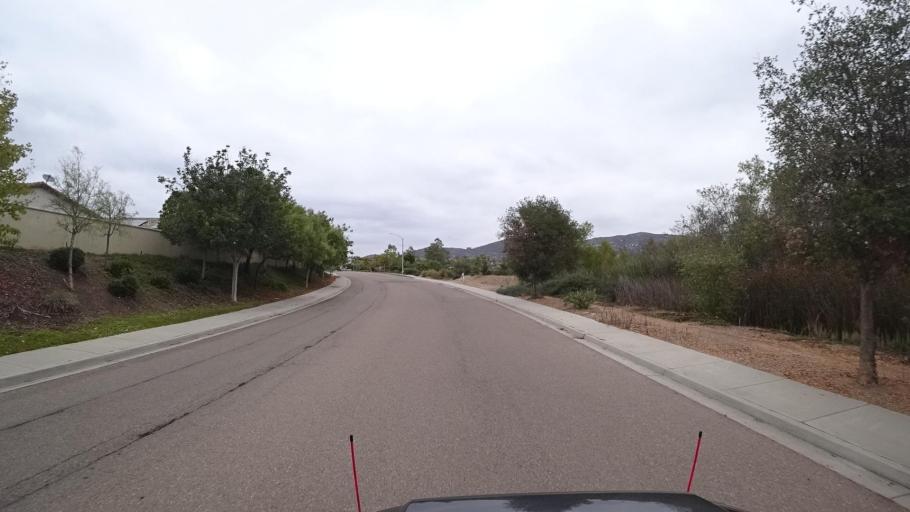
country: US
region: California
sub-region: San Diego County
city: Fairbanks Ranch
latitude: 33.0248
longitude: -117.1191
